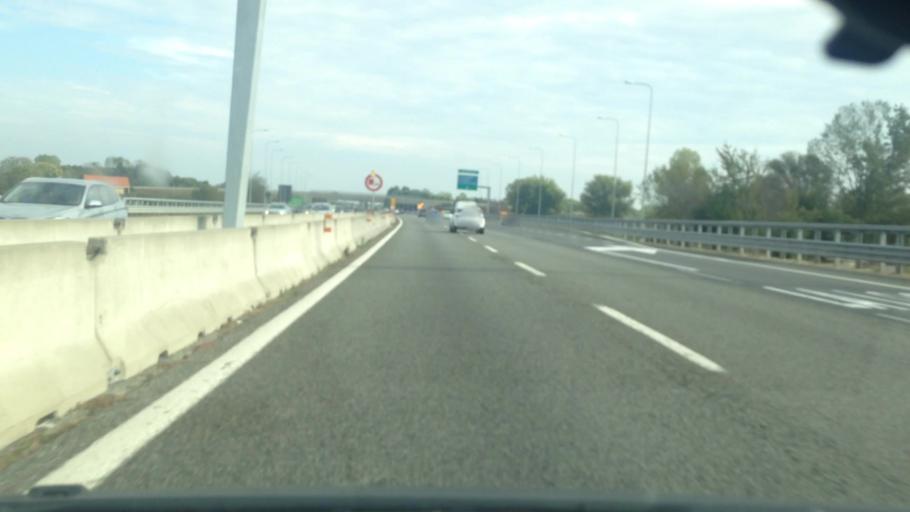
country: IT
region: Piedmont
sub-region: Provincia di Torino
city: Tagliaferro
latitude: 44.9738
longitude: 7.6612
